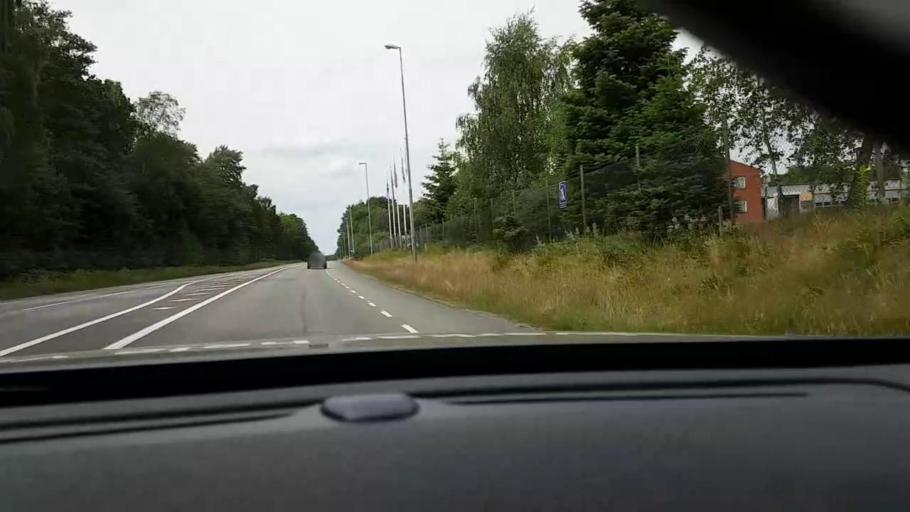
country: SE
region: Skane
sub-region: Hassleholms Kommun
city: Hassleholm
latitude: 56.1584
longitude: 13.7438
